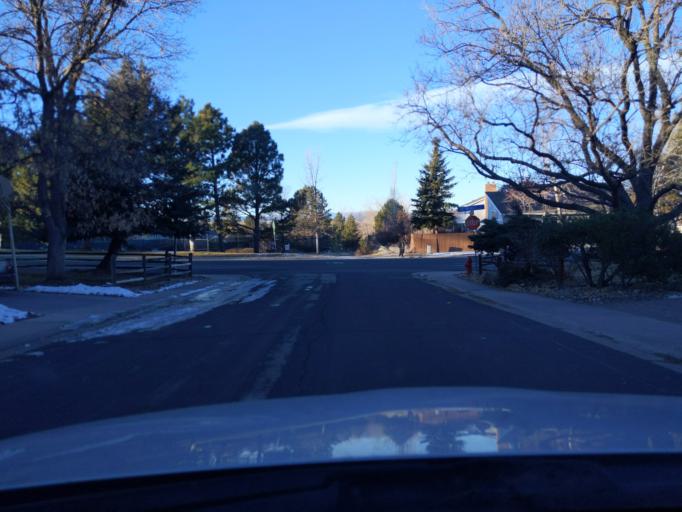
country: US
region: Colorado
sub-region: Arapahoe County
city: Castlewood
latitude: 39.5729
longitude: -104.8911
